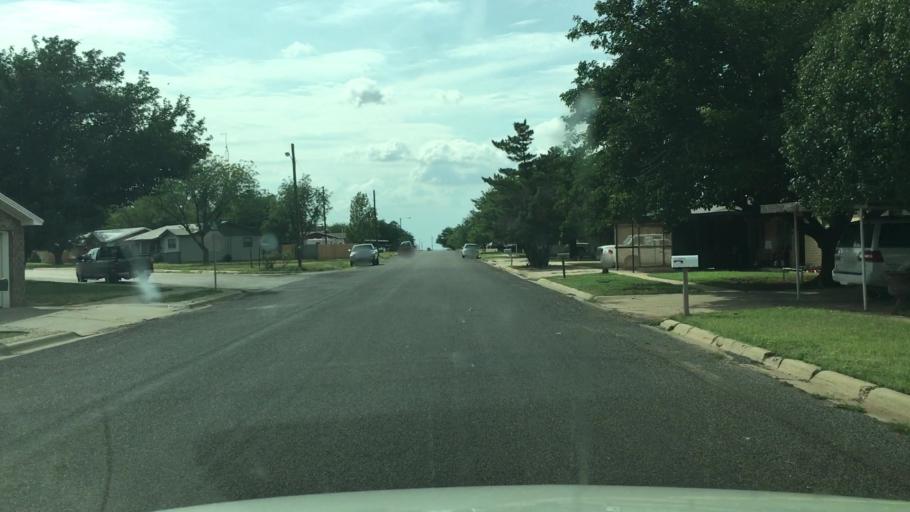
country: US
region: Texas
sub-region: Dawson County
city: Lamesa
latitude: 32.7518
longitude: -101.9527
